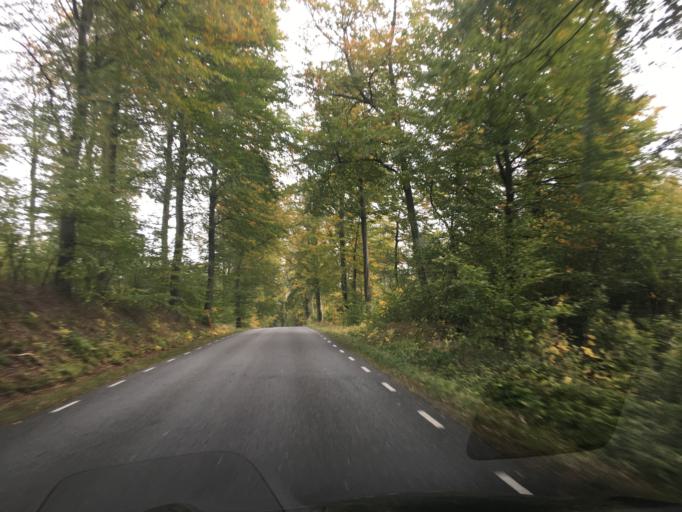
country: SE
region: Skane
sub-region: Tomelilla Kommun
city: Tomelilla
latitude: 55.6434
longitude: 14.0506
